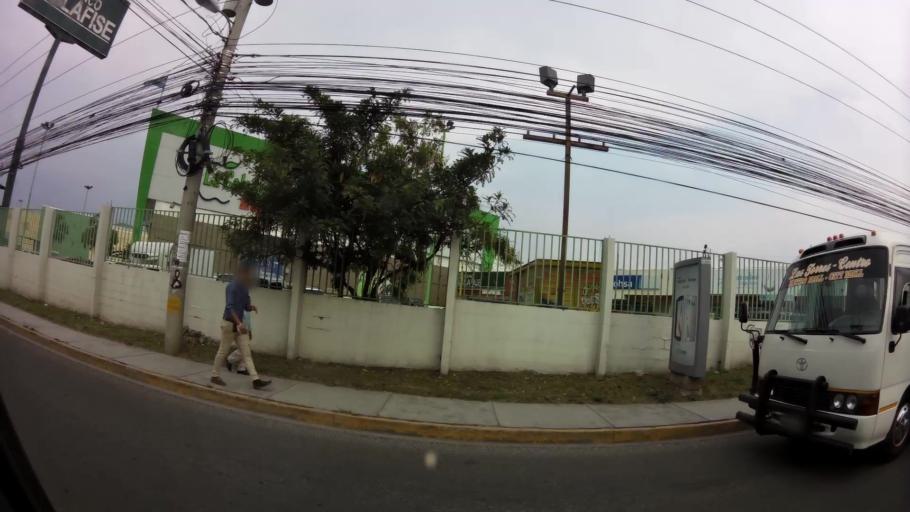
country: HN
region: Francisco Morazan
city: Tegucigalpa
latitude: 14.0627
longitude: -87.2231
